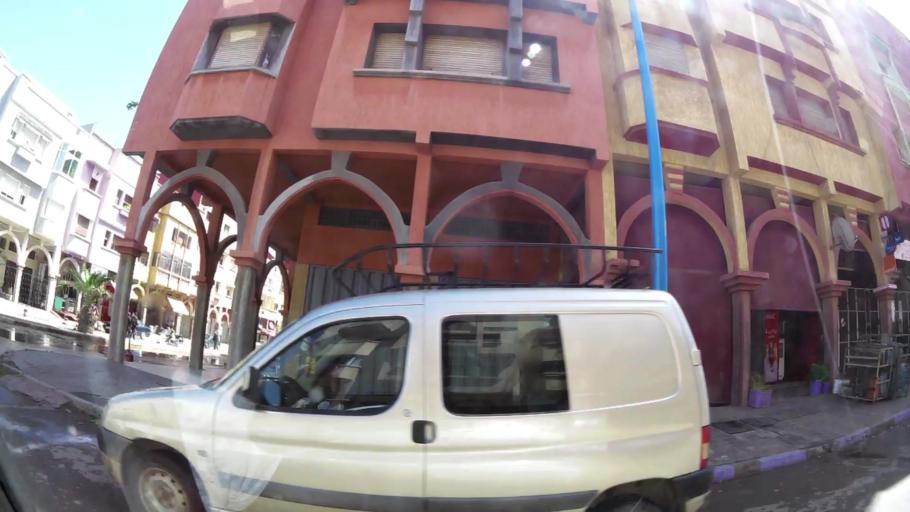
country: MA
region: Grand Casablanca
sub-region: Mohammedia
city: Mohammedia
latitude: 33.6388
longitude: -7.4529
